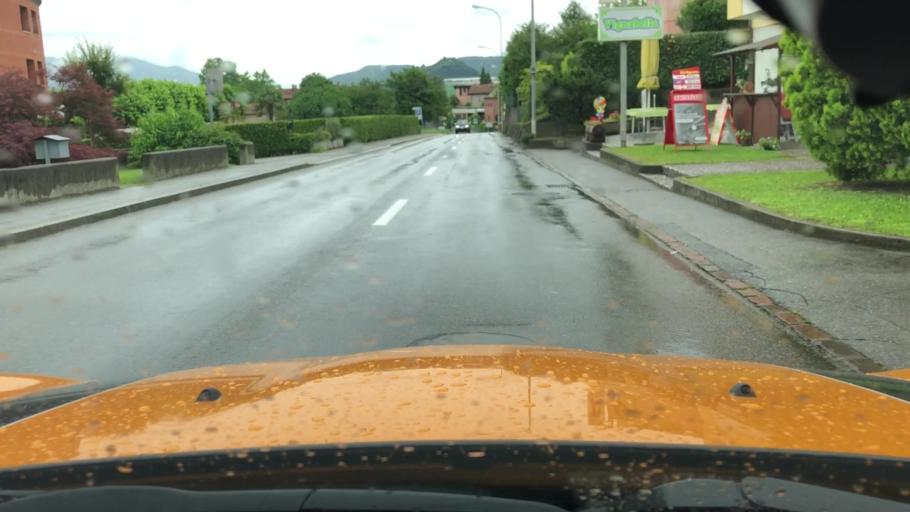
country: CH
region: Ticino
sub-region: Mendrisio District
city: Novazzano
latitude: 45.8425
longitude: 8.9745
